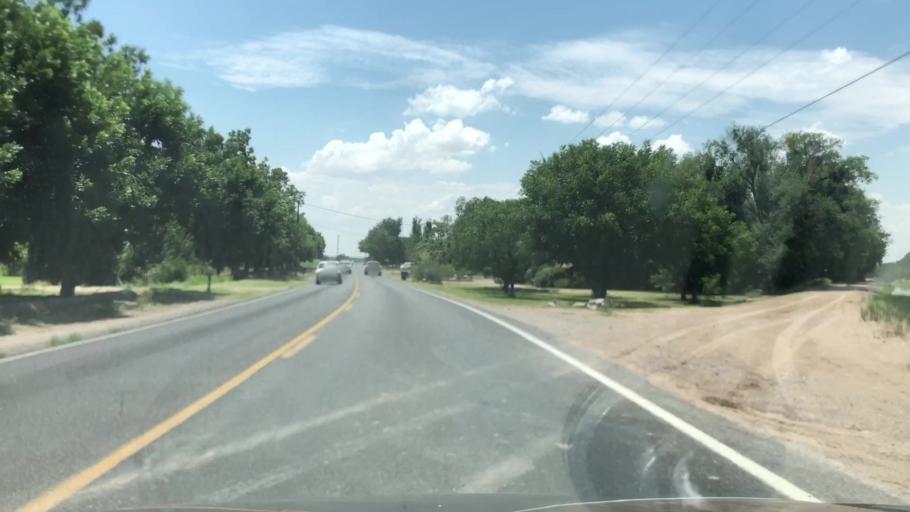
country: US
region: New Mexico
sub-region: Dona Ana County
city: La Union
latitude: 31.9822
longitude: -106.6514
